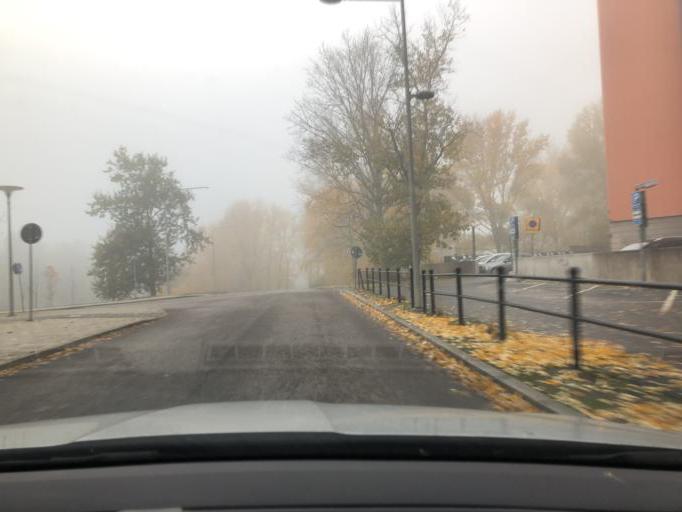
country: SE
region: Stockholm
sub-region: Botkyrka Kommun
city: Tullinge
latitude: 59.2235
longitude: 17.9370
